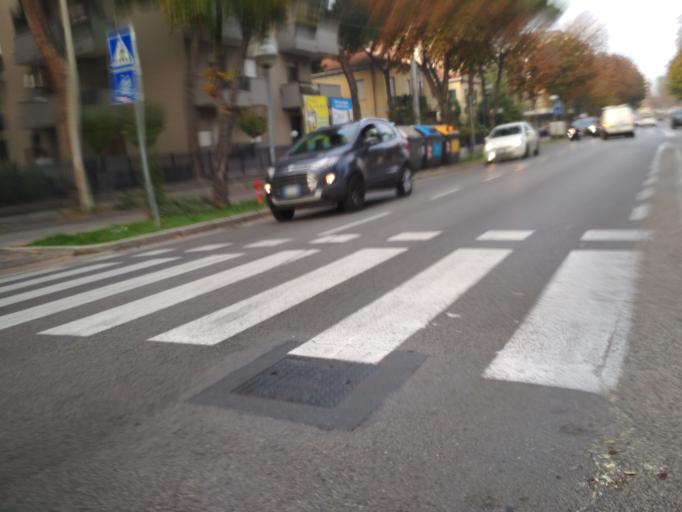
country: IT
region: Emilia-Romagna
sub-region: Provincia di Rimini
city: Rimini
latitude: 44.0576
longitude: 12.5609
